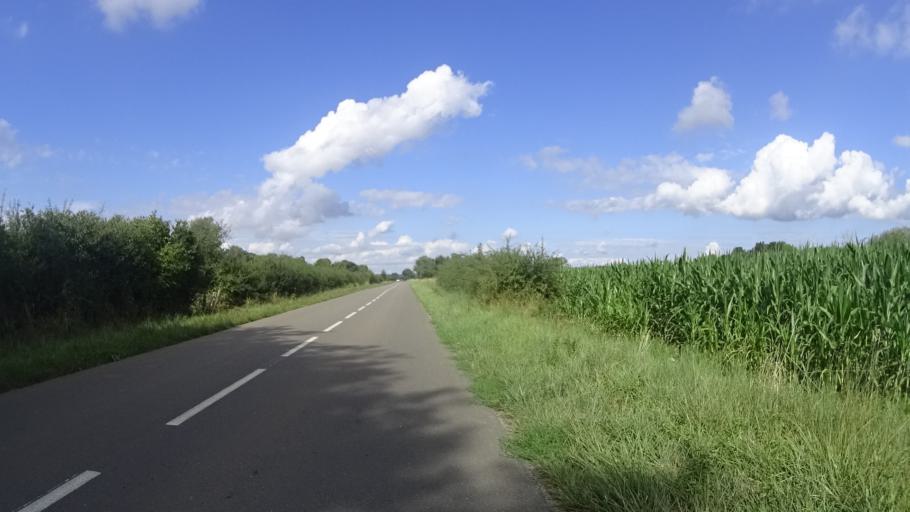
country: FR
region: Franche-Comte
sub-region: Departement du Jura
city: Orchamps
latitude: 47.1371
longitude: 5.6647
